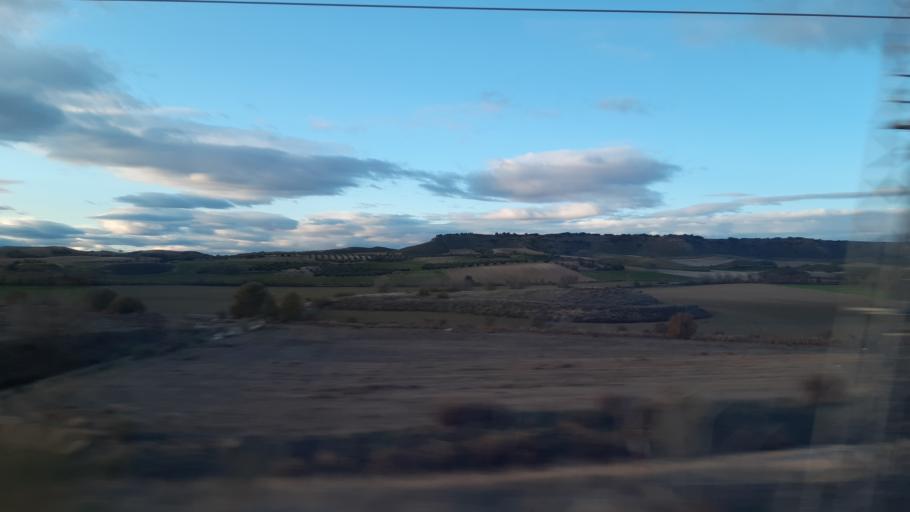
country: ES
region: Madrid
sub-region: Provincia de Madrid
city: Villalbilla
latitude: 40.4573
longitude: -3.3097
